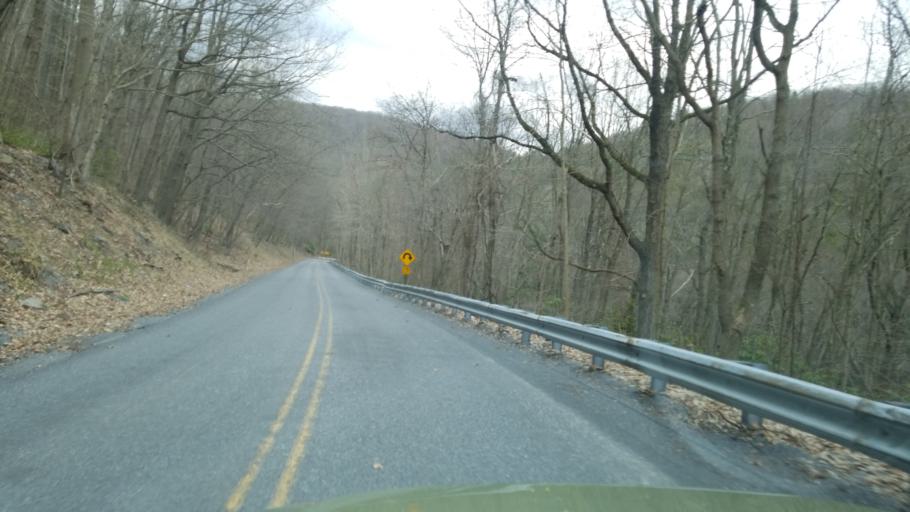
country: US
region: Pennsylvania
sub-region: Blair County
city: Tipton
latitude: 40.6914
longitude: -78.3326
